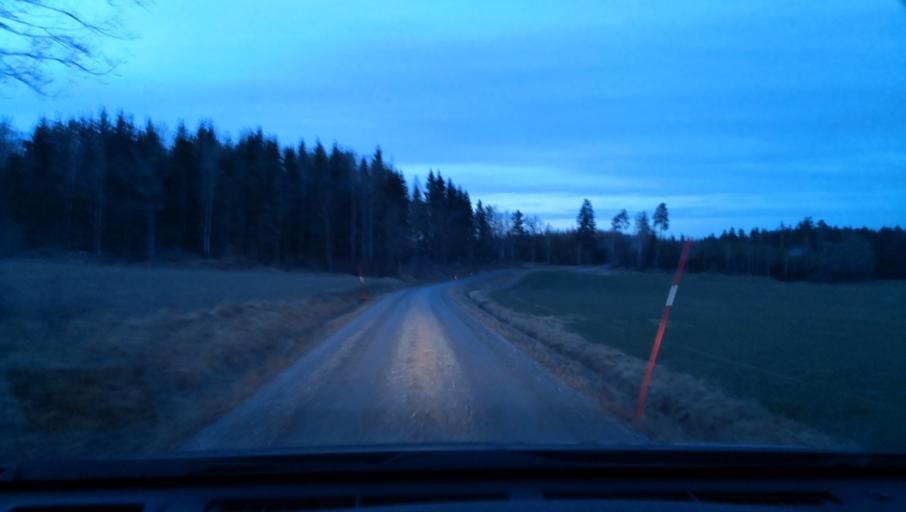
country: SE
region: Uppsala
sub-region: Enkopings Kommun
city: Dalby
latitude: 59.5597
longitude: 17.3711
